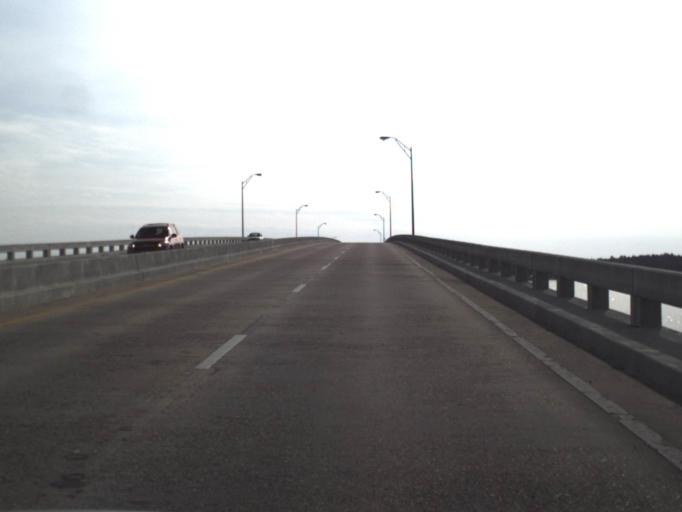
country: US
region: Florida
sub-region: Bay County
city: Tyndall Air Force Base
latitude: 30.1066
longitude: -85.6066
